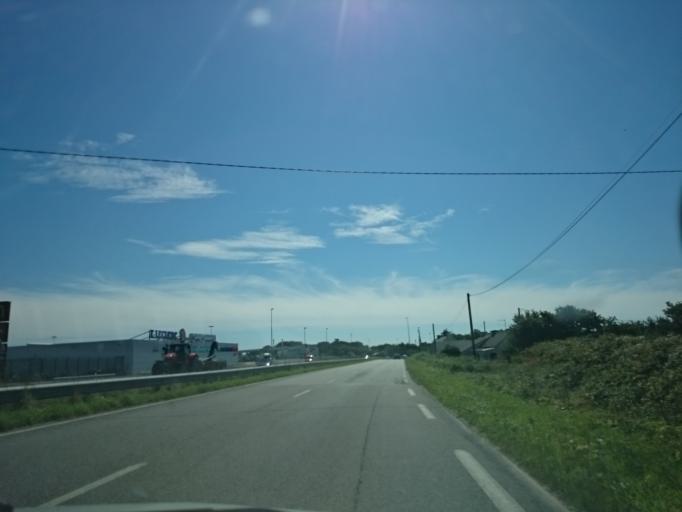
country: FR
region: Brittany
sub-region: Departement du Finistere
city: Guilers
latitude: 48.4272
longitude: -4.5746
